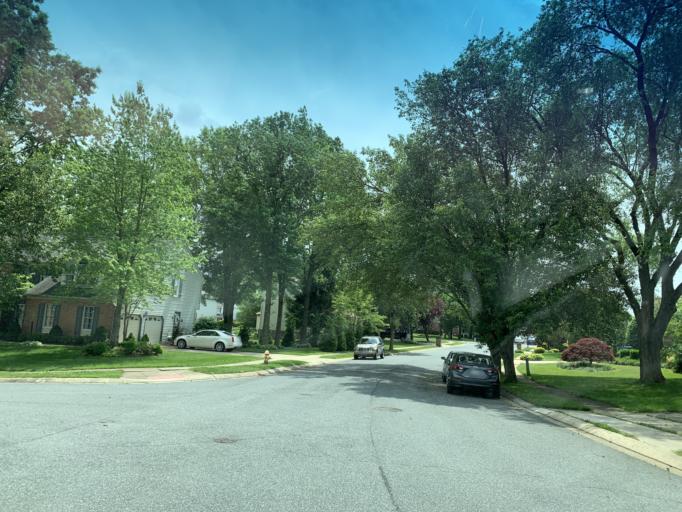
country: US
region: Maryland
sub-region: Harford County
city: South Bel Air
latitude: 39.5582
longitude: -76.3352
